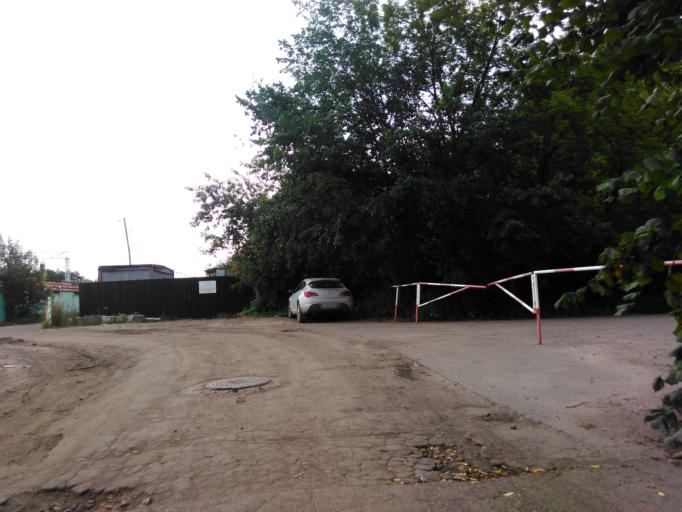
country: RU
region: Moskovskaya
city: Bogorodskoye
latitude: 55.8288
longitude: 37.7024
